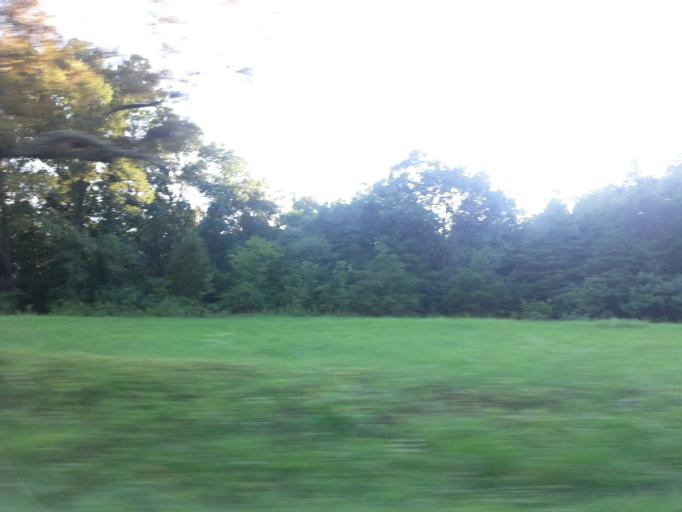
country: US
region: Tennessee
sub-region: Loudon County
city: Greenback
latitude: 35.6996
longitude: -84.2321
